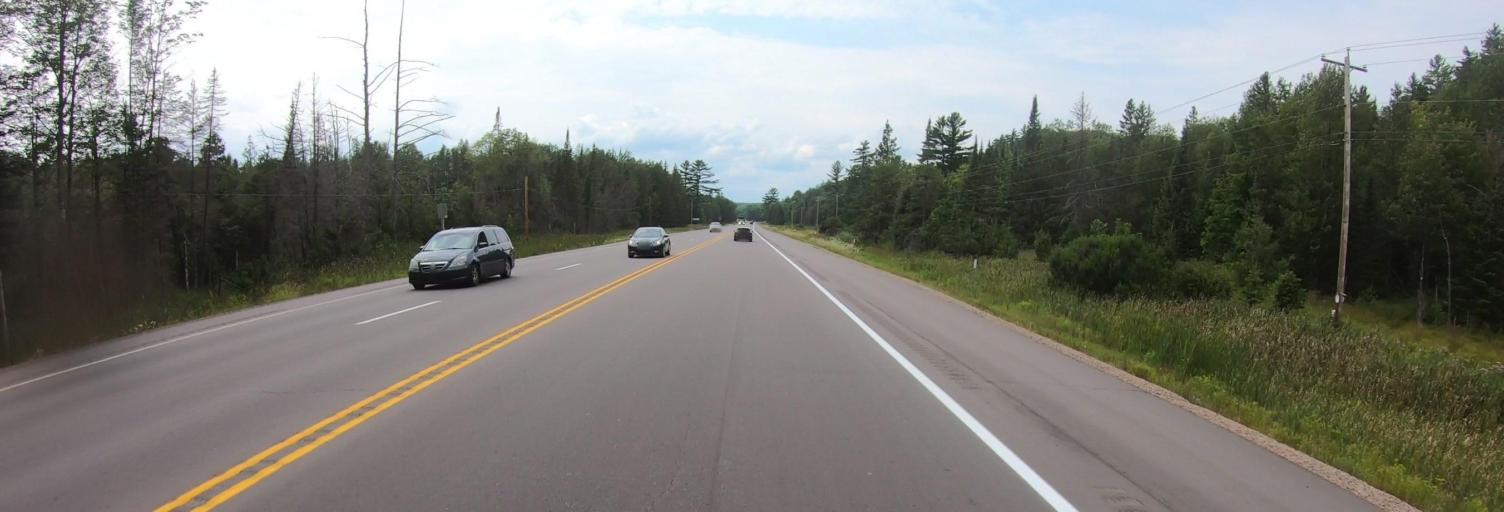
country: US
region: Michigan
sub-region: Marquette County
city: West Ishpeming
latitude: 46.5390
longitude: -88.0332
